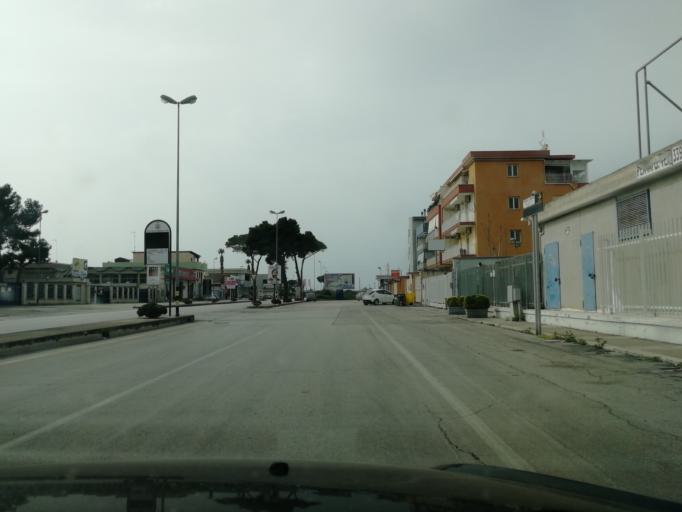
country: IT
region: Apulia
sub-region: Provincia di Barletta - Andria - Trani
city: Barletta
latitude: 41.3111
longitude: 16.3082
